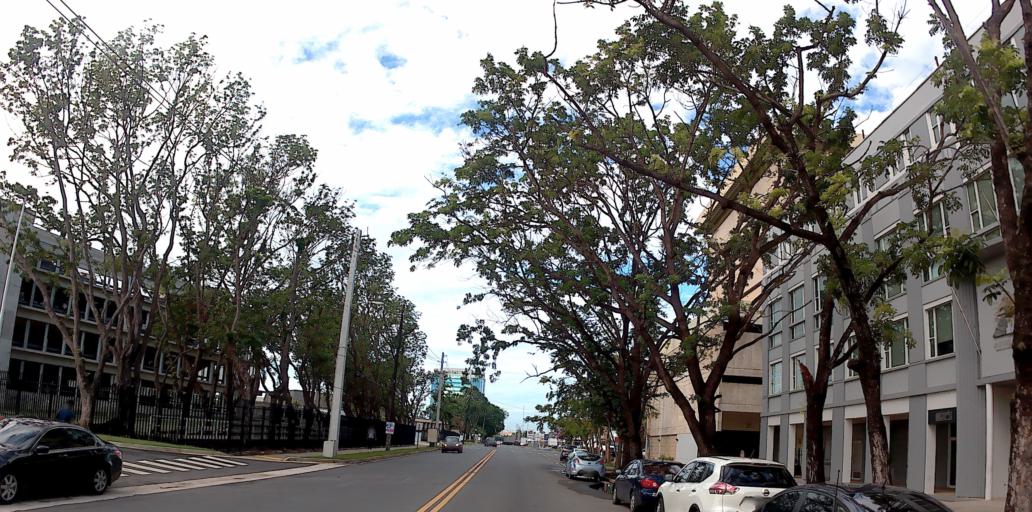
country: PR
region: Catano
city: Catano
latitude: 18.4252
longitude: -66.0627
